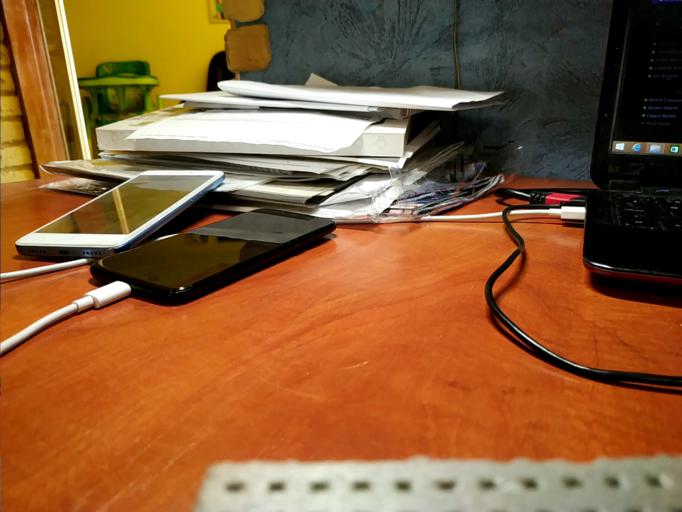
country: RU
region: Tverskaya
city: Spirovo
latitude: 57.4200
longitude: 35.1109
